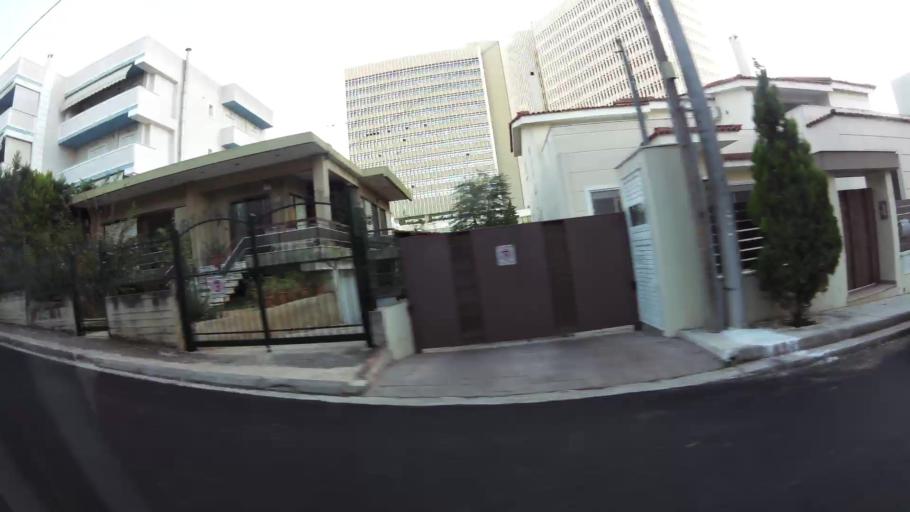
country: GR
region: Attica
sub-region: Nomarchia Athinas
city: Marousi
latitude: 38.0455
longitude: 23.8023
